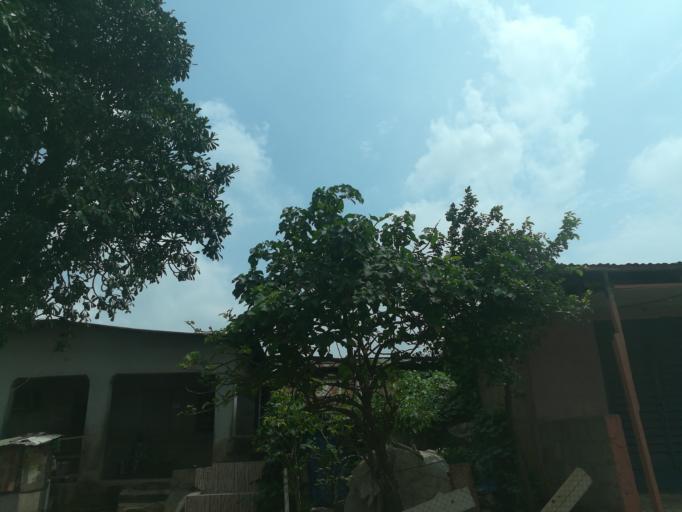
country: NG
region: Lagos
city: Ikorodu
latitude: 6.6096
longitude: 3.5051
